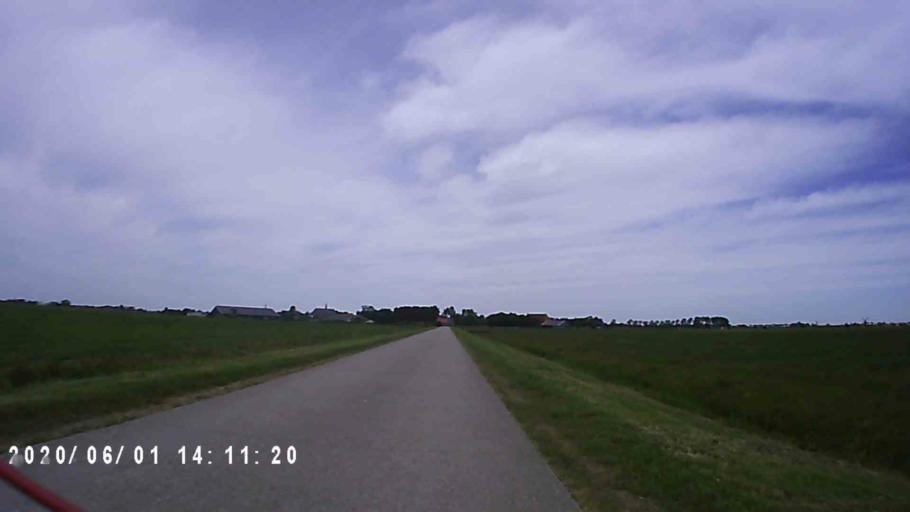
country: NL
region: Friesland
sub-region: Gemeente Littenseradiel
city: Winsum
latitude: 53.1266
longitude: 5.6493
